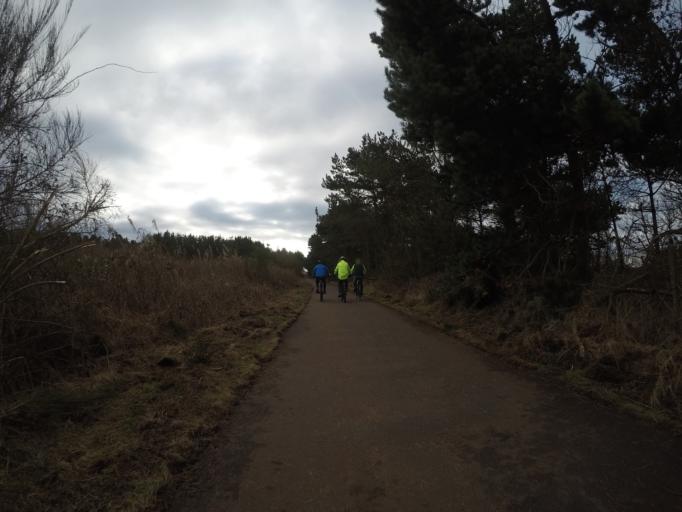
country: GB
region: Scotland
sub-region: North Ayrshire
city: Irvine
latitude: 55.5916
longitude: -4.6696
